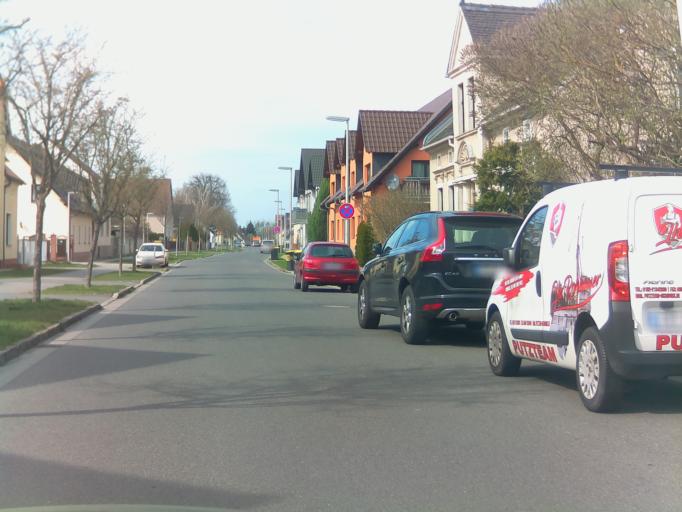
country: DE
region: Brandenburg
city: Cottbus
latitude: 51.7550
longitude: 14.3025
